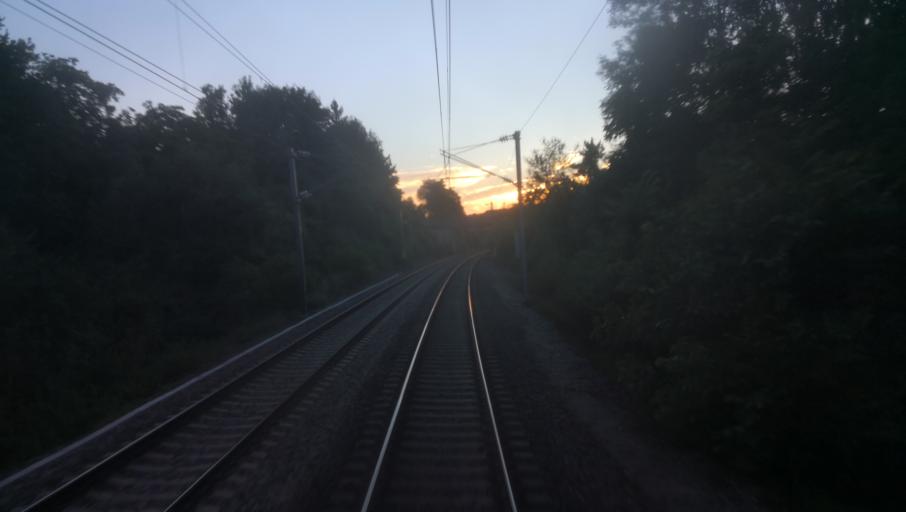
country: FR
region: Ile-de-France
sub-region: Departement des Yvelines
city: Breval
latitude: 48.9168
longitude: 1.4944
